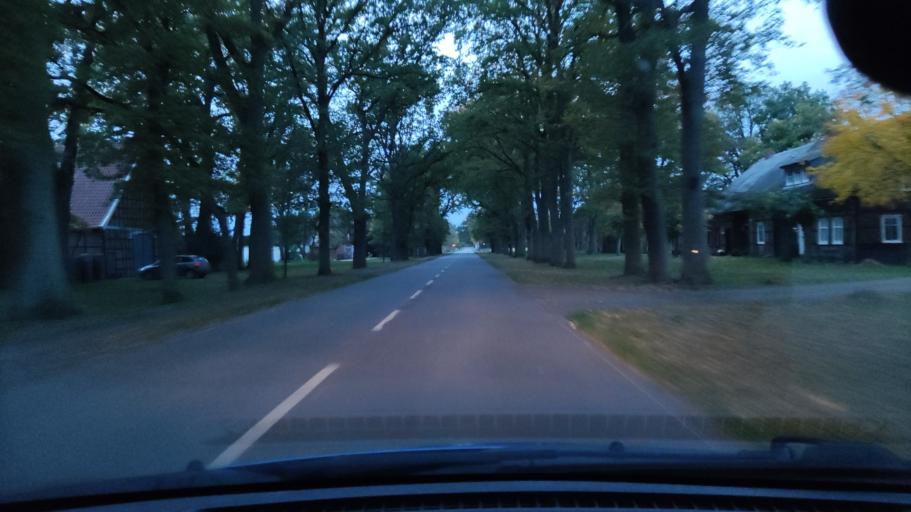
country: DE
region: Lower Saxony
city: Trebel
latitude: 52.9588
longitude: 11.3280
